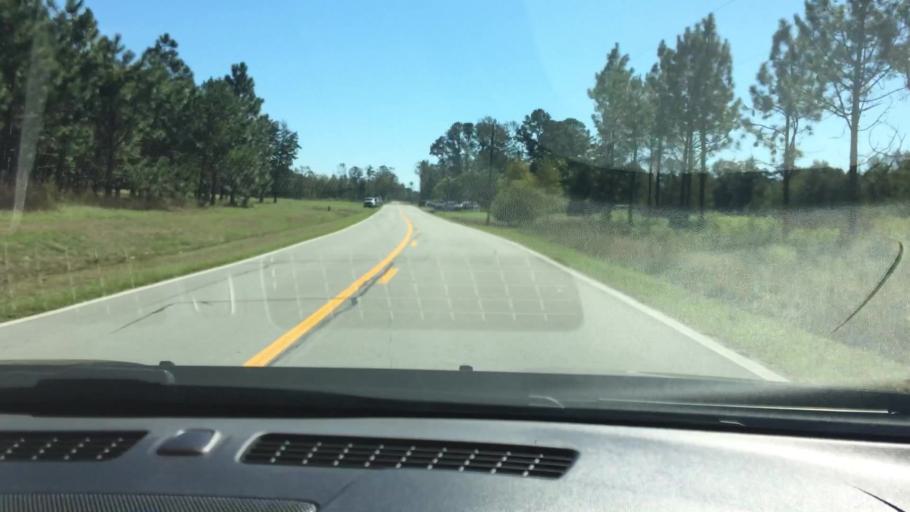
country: US
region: North Carolina
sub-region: Craven County
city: Vanceboro
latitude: 35.3242
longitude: -77.2961
